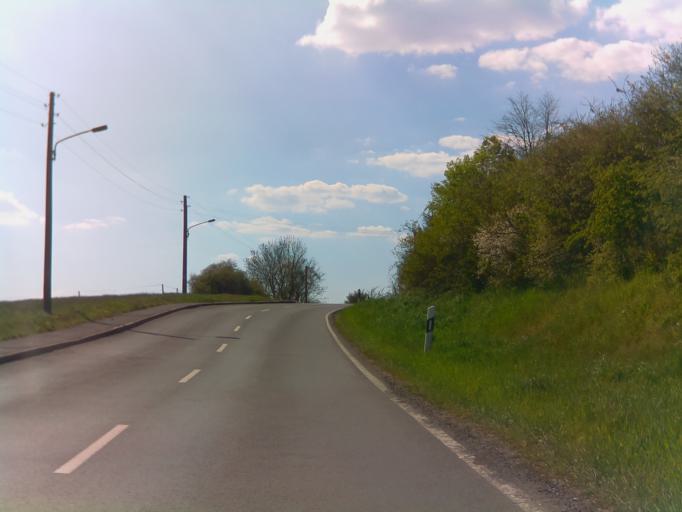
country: DE
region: Thuringia
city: Zeulenroda
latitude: 50.6254
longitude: 12.0323
